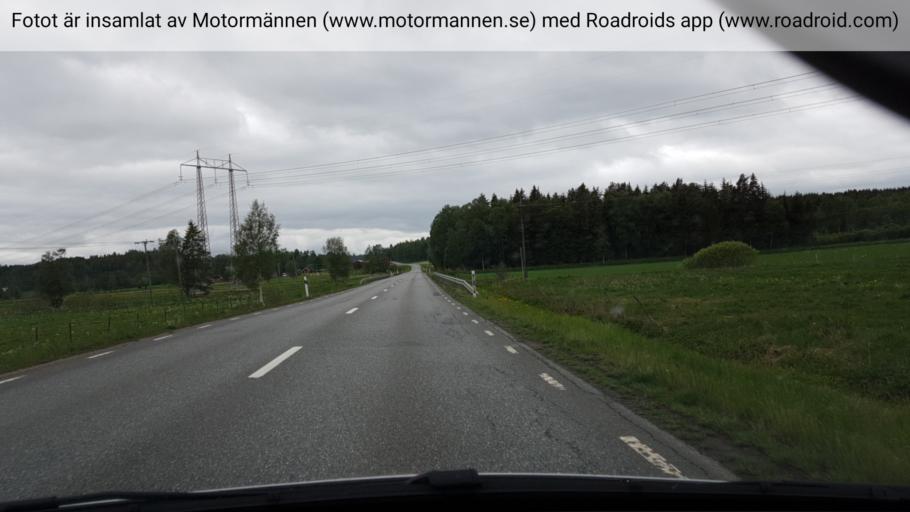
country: SE
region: Joenkoeping
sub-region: Aneby Kommun
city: Aneby
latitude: 57.9808
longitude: 14.8260
